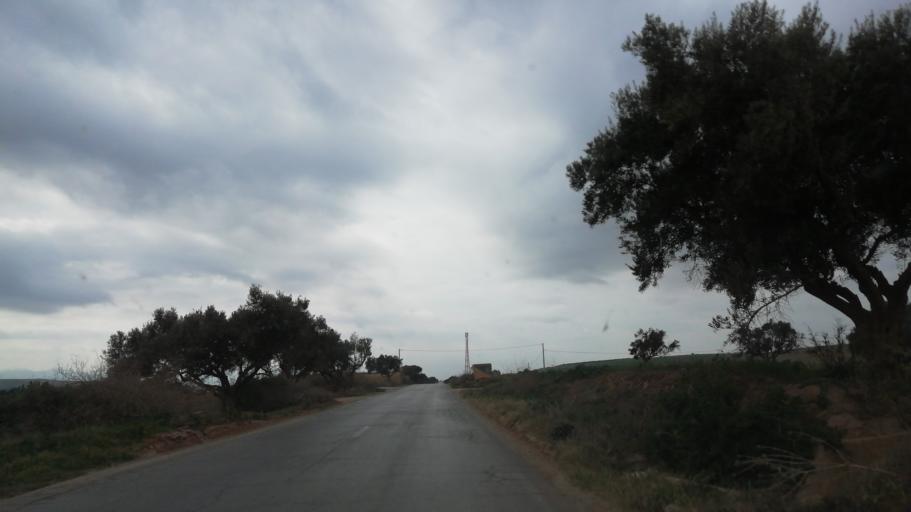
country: DZ
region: Oran
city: Sidi ech Chahmi
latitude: 35.6146
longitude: -0.4209
